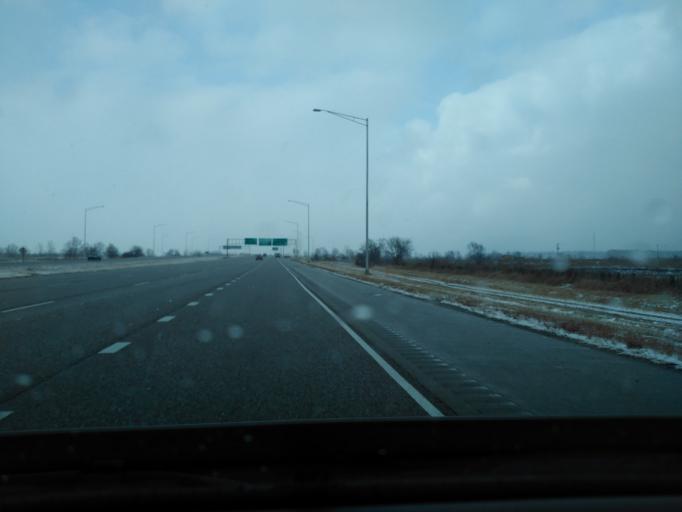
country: US
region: Illinois
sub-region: Saint Clair County
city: Caseyville
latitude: 38.6668
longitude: -90.0291
